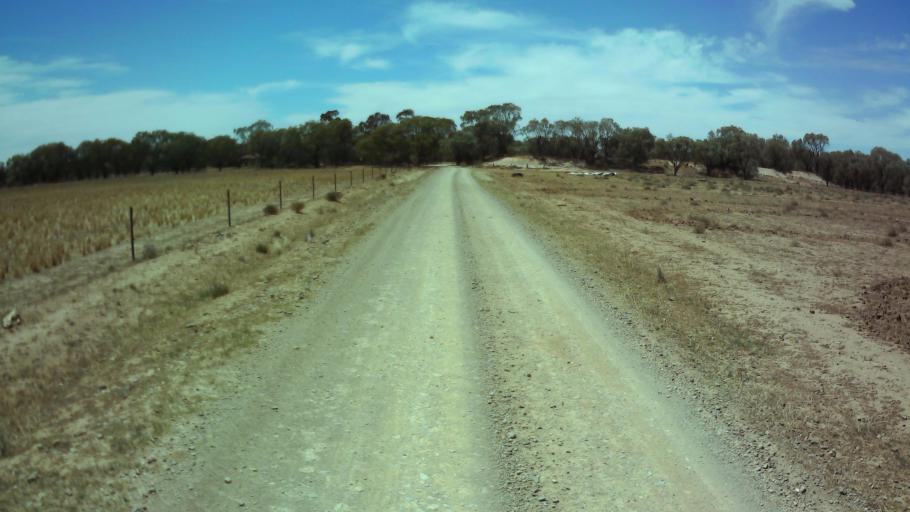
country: AU
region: New South Wales
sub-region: Weddin
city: Grenfell
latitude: -33.8679
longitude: 147.7671
